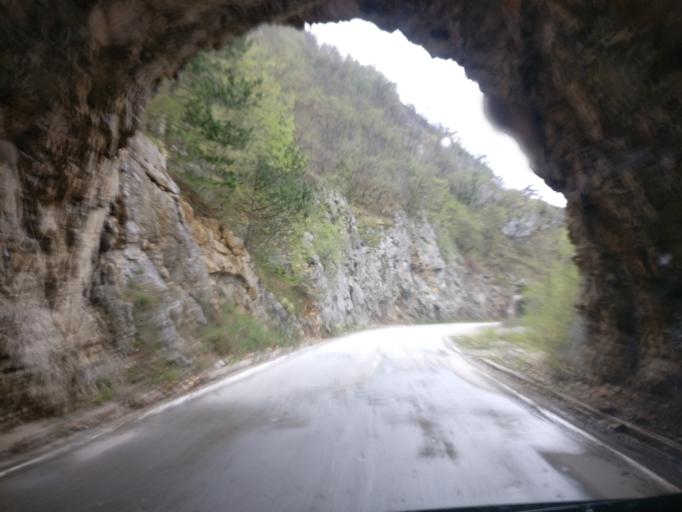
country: ME
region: Opstina Pluzine
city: Pluzine
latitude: 43.2498
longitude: 18.8324
